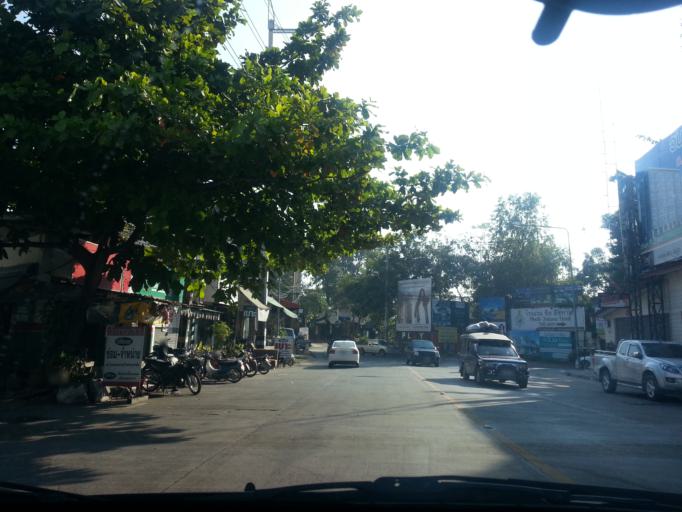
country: TH
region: Chiang Mai
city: Chiang Mai
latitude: 18.7612
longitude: 98.9973
